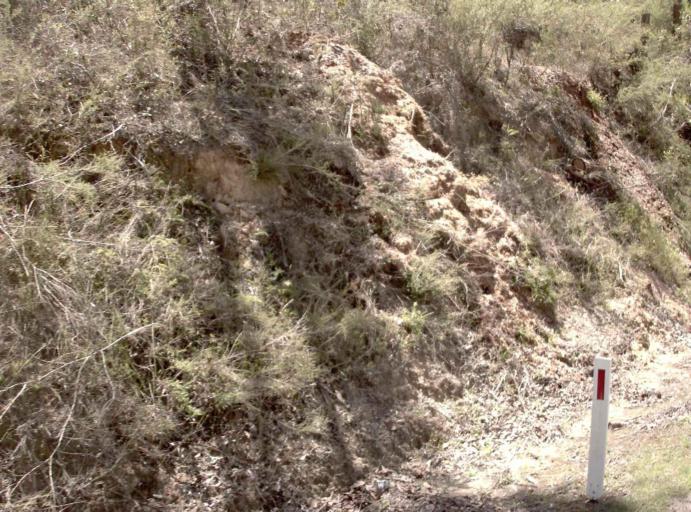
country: AU
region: New South Wales
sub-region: Bombala
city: Bombala
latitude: -37.6196
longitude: 148.8914
